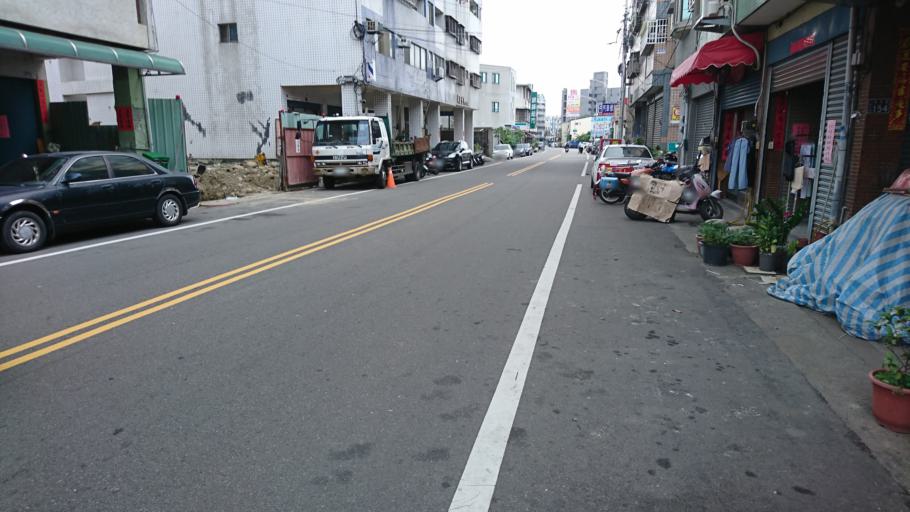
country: TW
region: Taiwan
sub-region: Taichung City
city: Taichung
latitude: 24.0794
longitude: 120.6944
